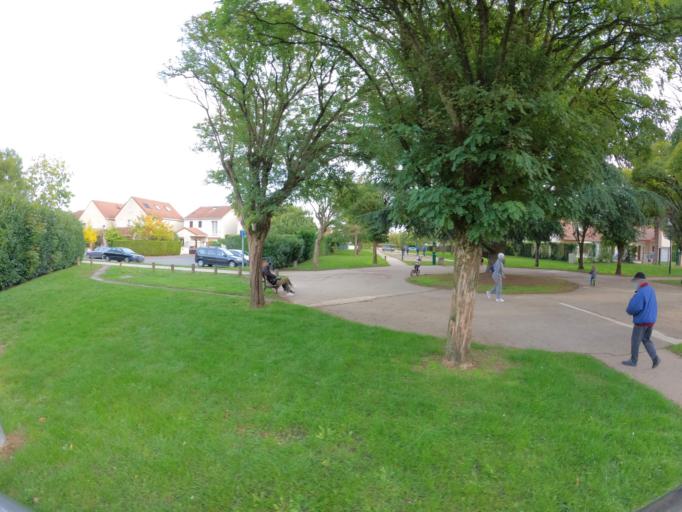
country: FR
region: Ile-de-France
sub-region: Departement de Seine-et-Marne
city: Pontault-Combault
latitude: 48.7958
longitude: 2.6137
